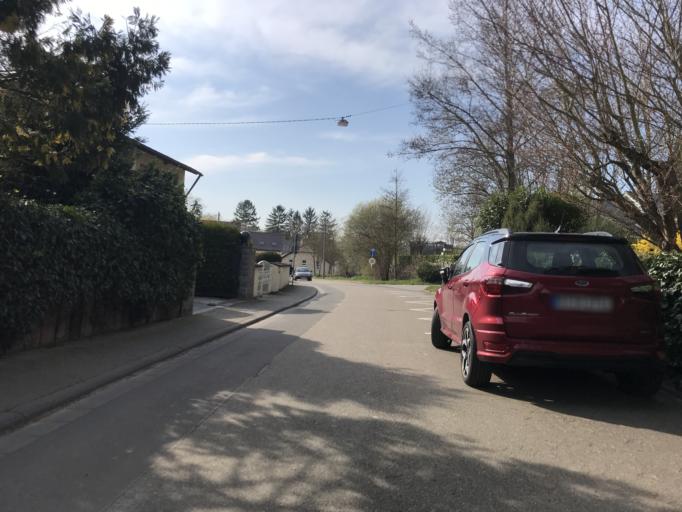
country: DE
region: Rheinland-Pfalz
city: Stadecken-Elsheim
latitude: 49.9161
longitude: 8.1191
